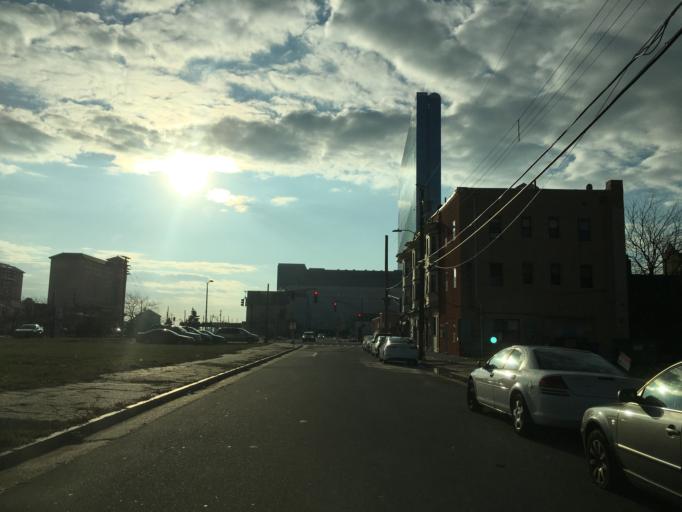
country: US
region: New Jersey
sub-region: Atlantic County
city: Atlantic City
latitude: 39.3674
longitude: -74.4173
